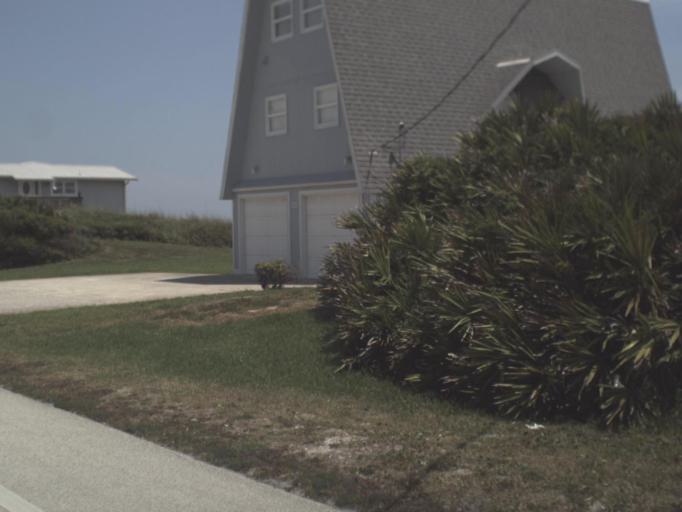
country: US
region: Florida
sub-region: Saint Johns County
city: Villano Beach
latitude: 29.9484
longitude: -81.3033
